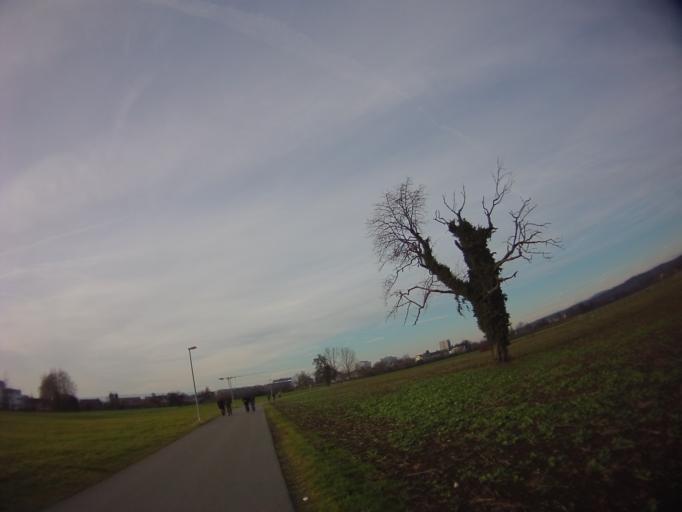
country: CH
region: Zug
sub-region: Zug
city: Zug
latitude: 47.1790
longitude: 8.4987
